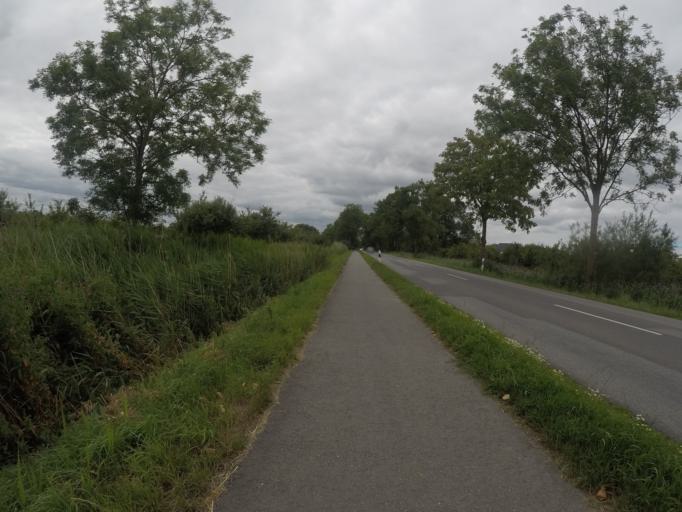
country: DE
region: Lower Saxony
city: Grossenworden
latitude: 53.6713
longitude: 9.2938
